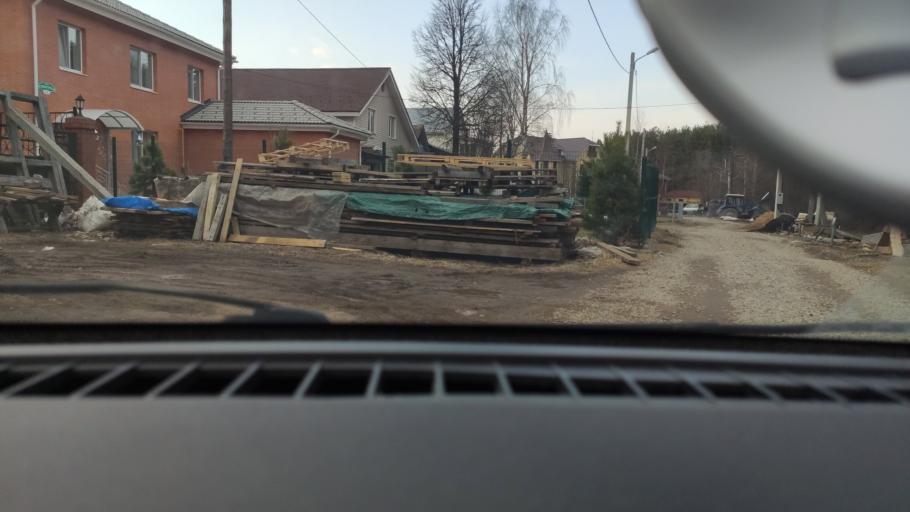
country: RU
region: Perm
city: Perm
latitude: 57.9826
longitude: 56.3120
